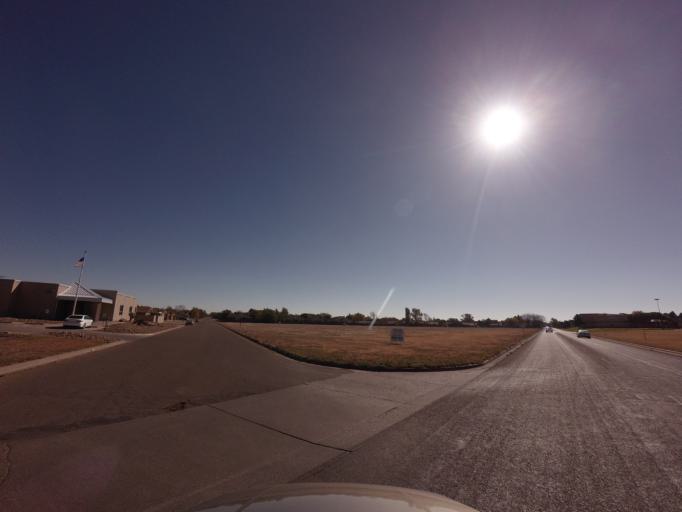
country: US
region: New Mexico
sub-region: Curry County
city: Clovis
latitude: 34.4261
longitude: -103.1920
